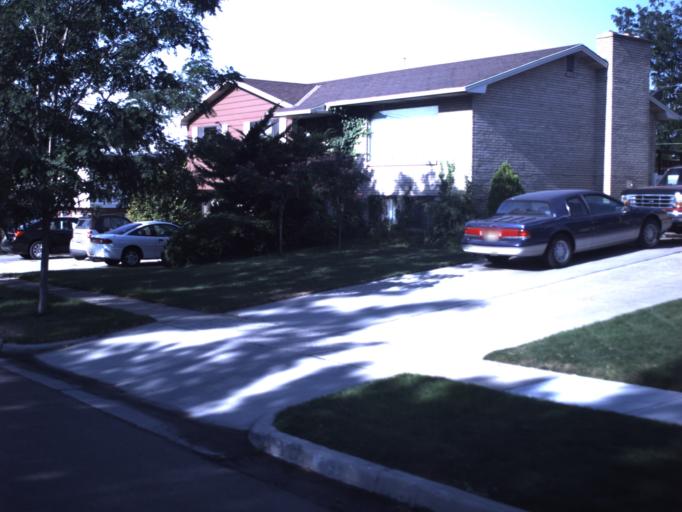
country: US
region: Utah
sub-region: Utah County
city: American Fork
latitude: 40.3929
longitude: -111.7959
